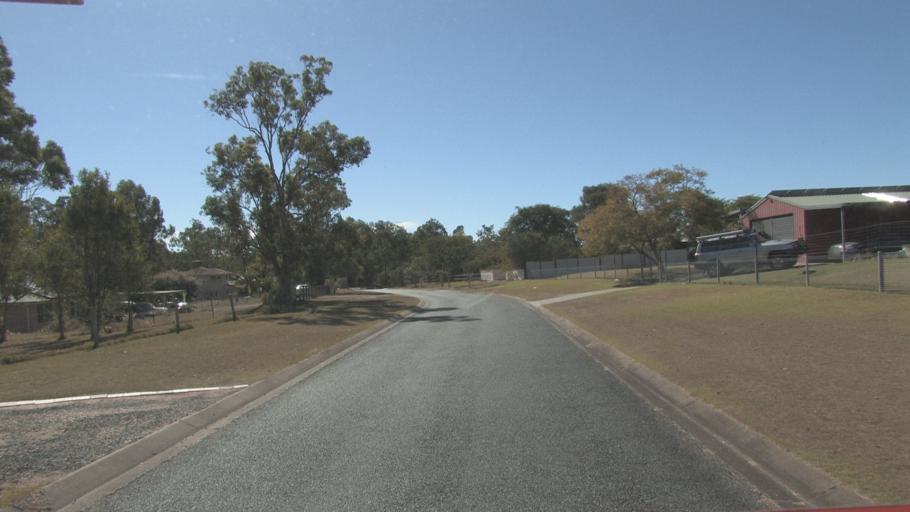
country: AU
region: Queensland
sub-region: Logan
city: North Maclean
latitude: -27.8206
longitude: 152.9501
